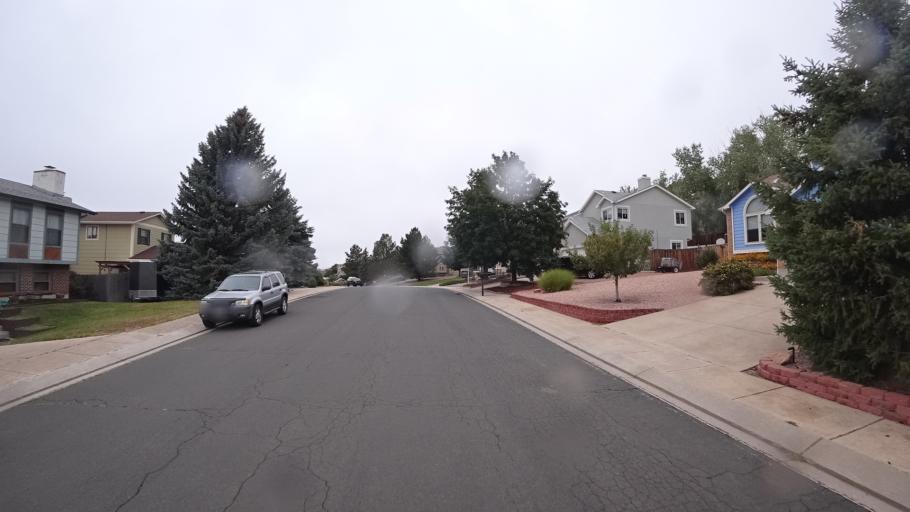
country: US
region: Colorado
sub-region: El Paso County
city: Cimarron Hills
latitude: 38.9340
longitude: -104.7624
